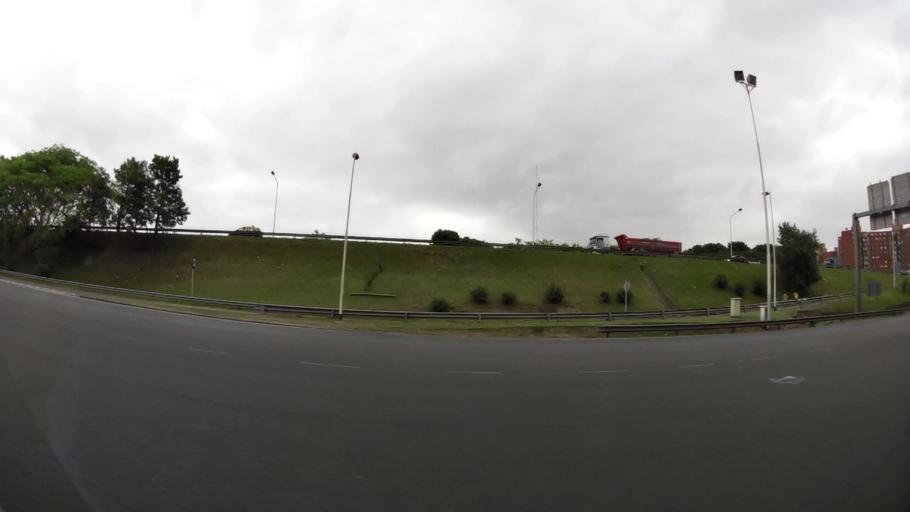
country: AR
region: Buenos Aires F.D.
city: Villa Lugano
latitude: -34.6960
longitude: -58.4931
